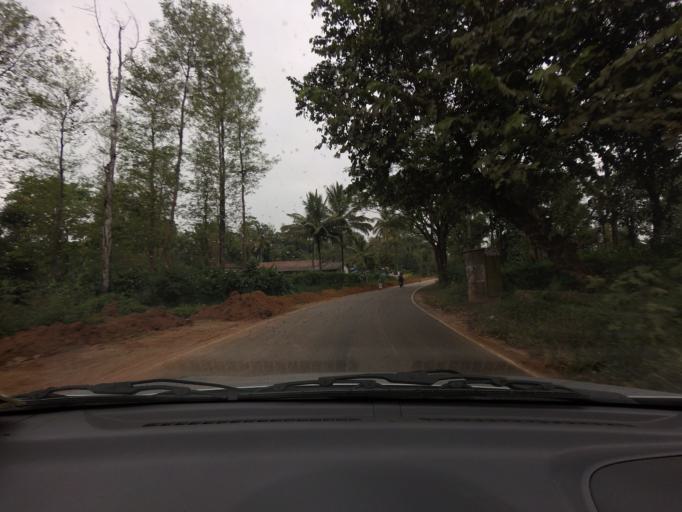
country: IN
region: Karnataka
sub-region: Hassan
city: Sakleshpur
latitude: 12.9562
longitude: 75.7434
